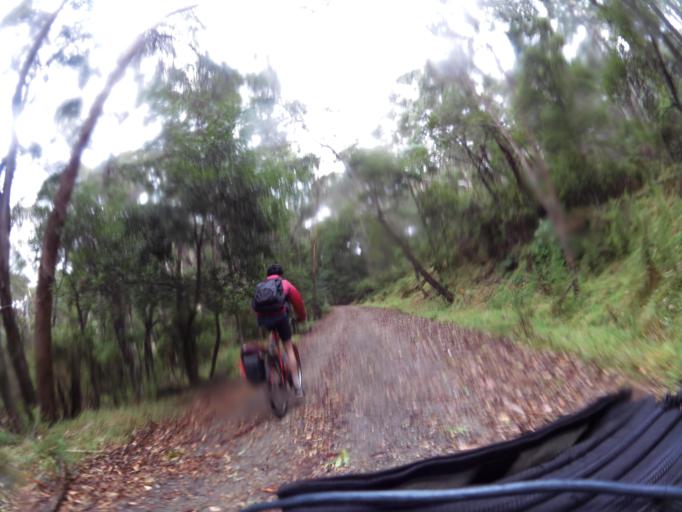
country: AU
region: New South Wales
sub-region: Greater Hume Shire
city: Holbrook
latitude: -36.1910
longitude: 147.5081
